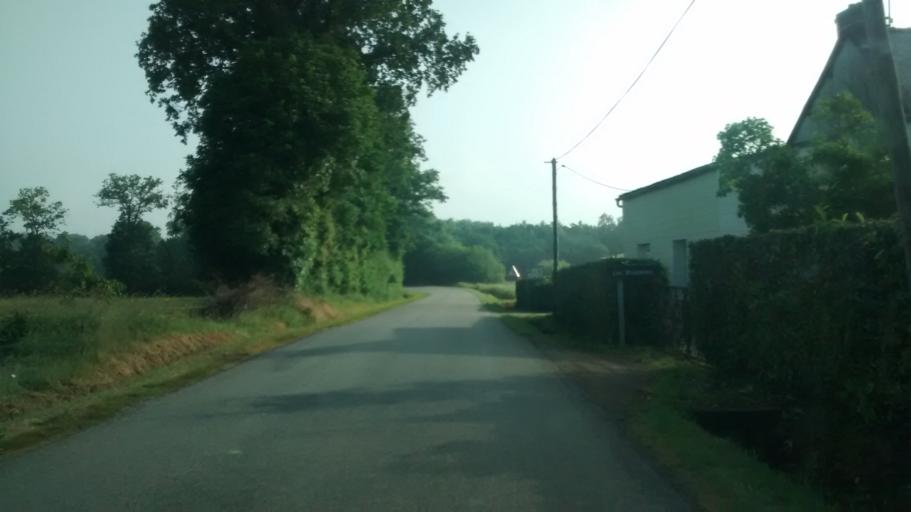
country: FR
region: Brittany
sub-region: Departement du Morbihan
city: Ruffiac
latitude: 47.8372
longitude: -2.2745
